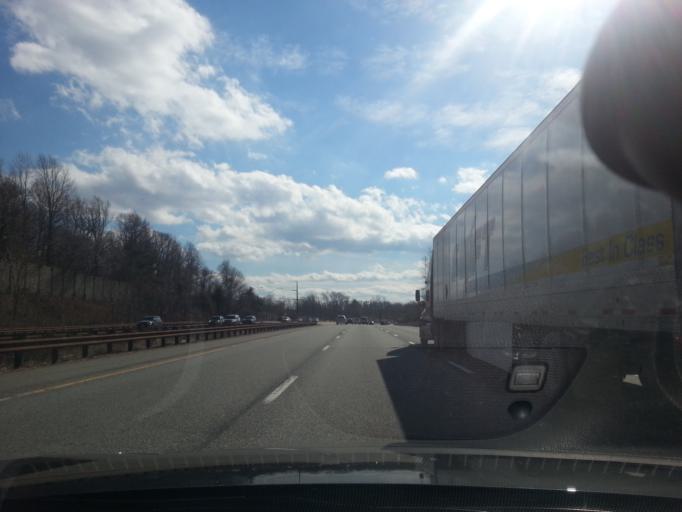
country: US
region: Pennsylvania
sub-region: Delaware County
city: Radnor
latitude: 40.0417
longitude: -75.3514
